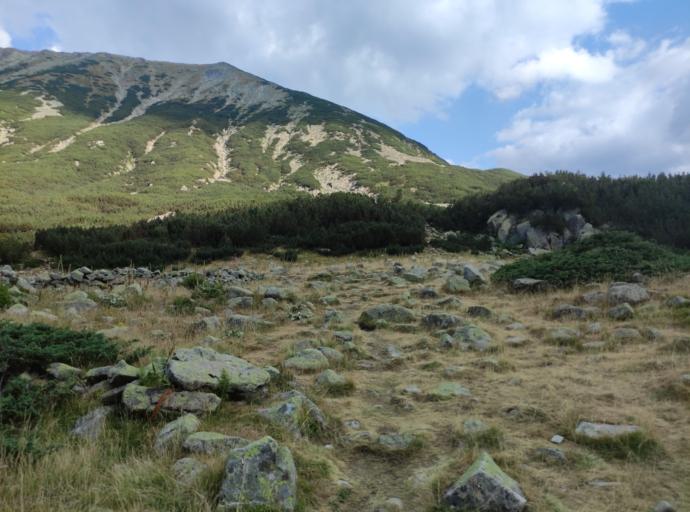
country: BG
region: Blagoevgrad
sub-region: Obshtina Bansko
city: Bansko
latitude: 41.7522
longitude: 23.4140
